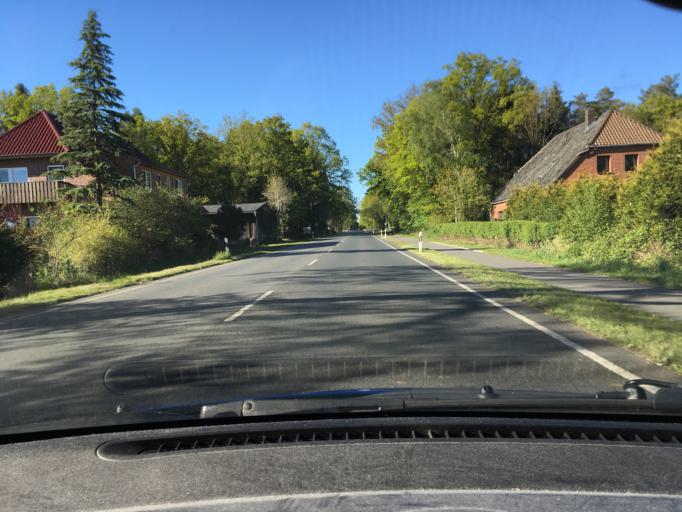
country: DE
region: Lower Saxony
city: Soltau
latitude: 53.0381
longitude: 9.8543
